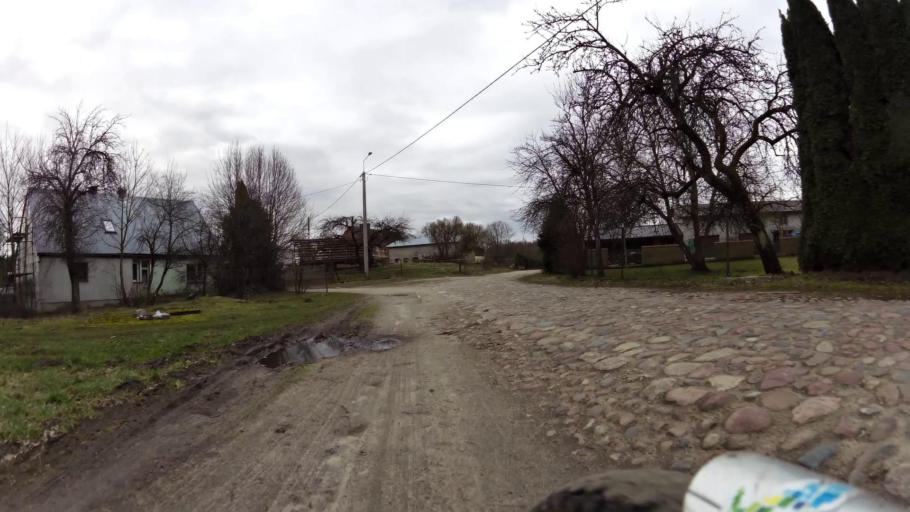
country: PL
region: Pomeranian Voivodeship
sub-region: Powiat bytowski
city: Trzebielino
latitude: 54.1067
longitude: 17.1301
